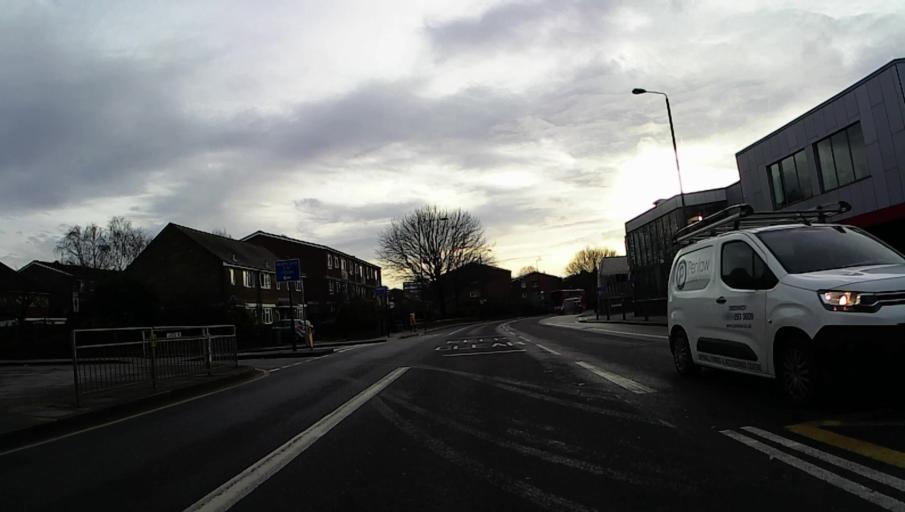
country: GB
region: England
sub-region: Greater London
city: Blackheath
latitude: 51.4896
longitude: 0.0088
